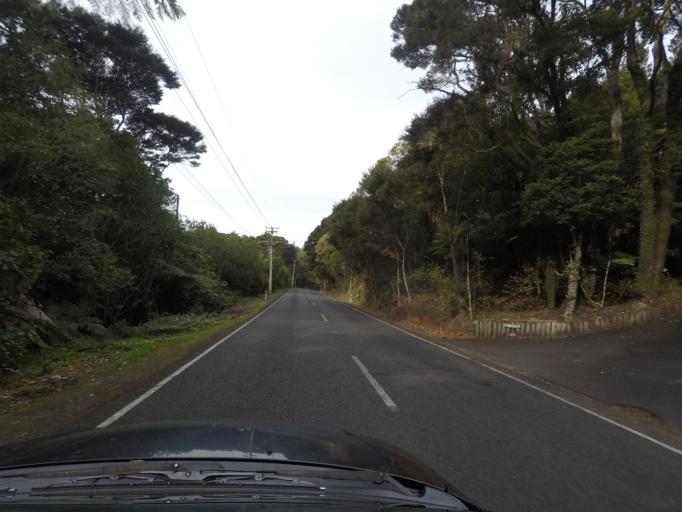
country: NZ
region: Auckland
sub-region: Auckland
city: Titirangi
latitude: -36.9388
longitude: 174.5804
